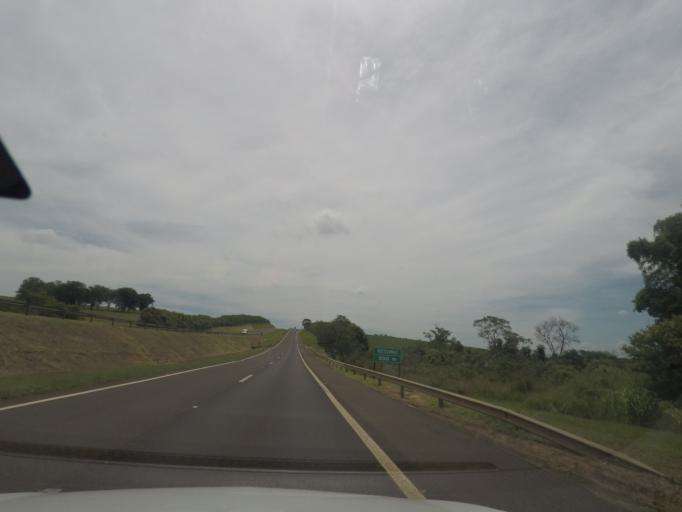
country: BR
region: Sao Paulo
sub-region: Bebedouro
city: Bebedouro
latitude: -21.0162
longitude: -48.4254
